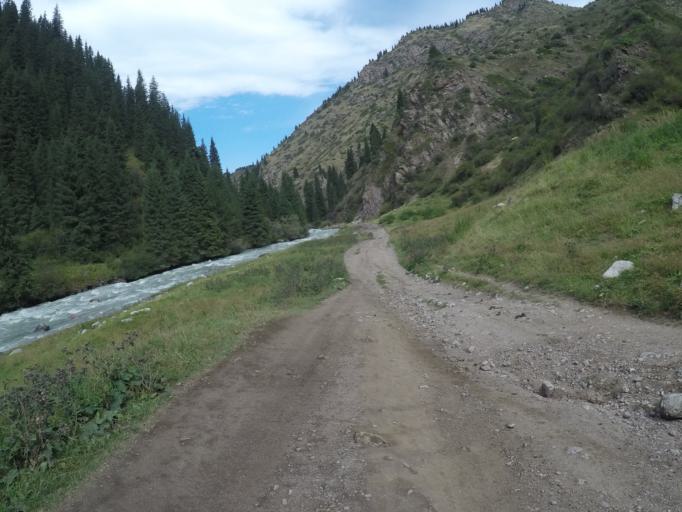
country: KG
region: Ysyk-Koel
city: Teploklyuchenka
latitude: 42.4392
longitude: 78.5581
